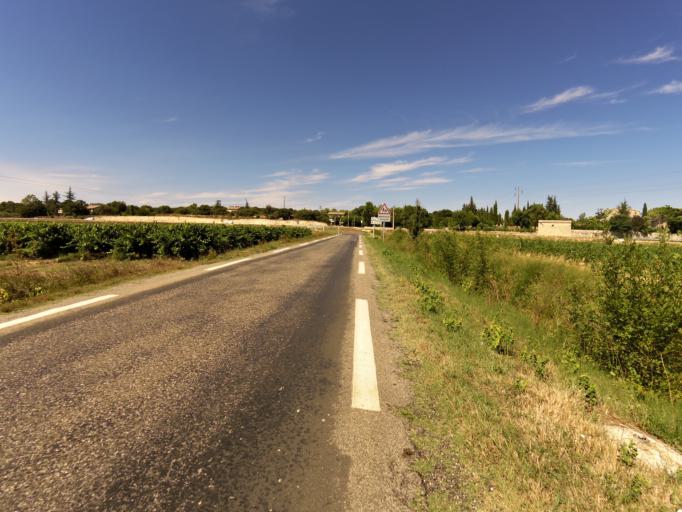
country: FR
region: Languedoc-Roussillon
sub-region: Departement du Gard
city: Quissac
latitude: 43.8822
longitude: 4.0470
